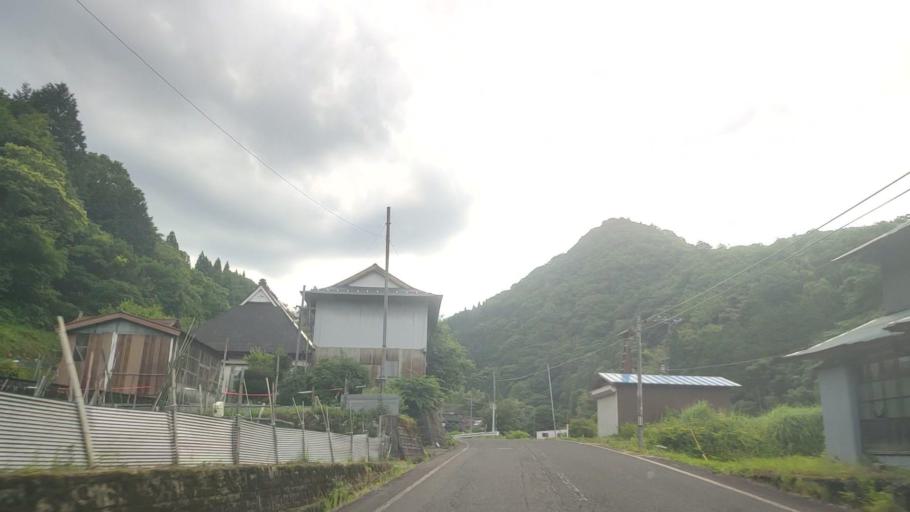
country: JP
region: Tottori
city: Kurayoshi
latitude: 35.3243
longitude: 134.0324
